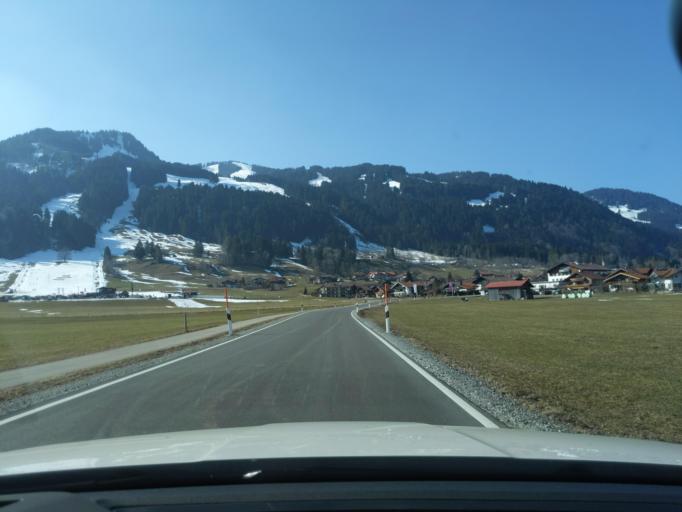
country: DE
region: Bavaria
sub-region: Swabia
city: Obermaiselstein
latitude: 47.4566
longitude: 10.2380
